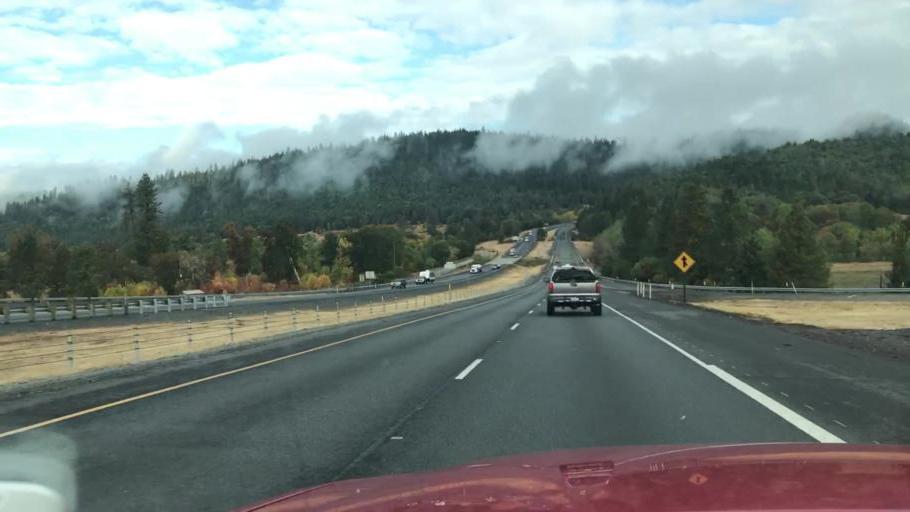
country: US
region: Oregon
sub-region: Josephine County
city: Merlin
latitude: 42.6321
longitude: -123.3821
